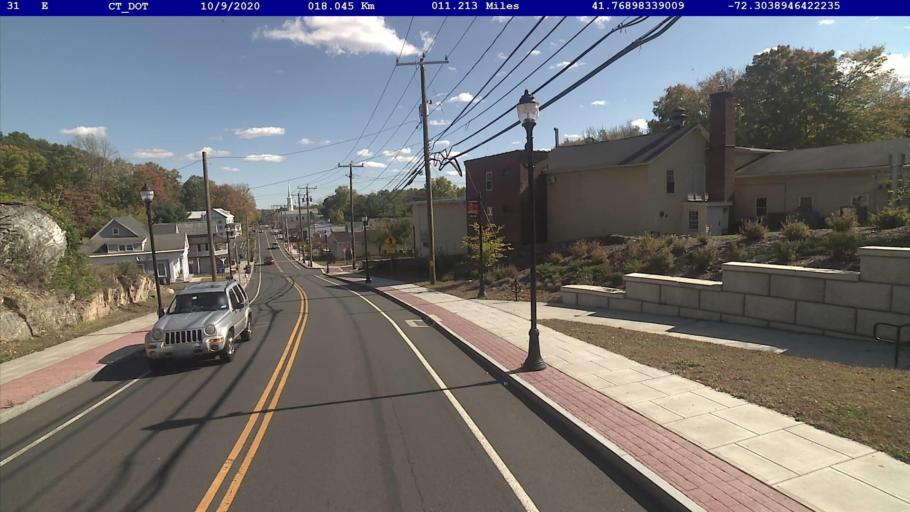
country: US
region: Connecticut
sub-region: Tolland County
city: South Coventry
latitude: 41.7690
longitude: -72.3039
